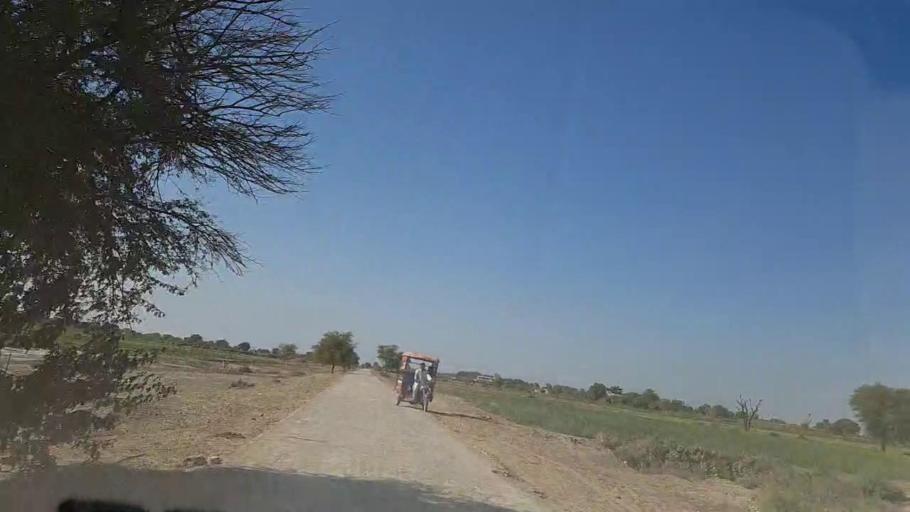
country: PK
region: Sindh
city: Digri
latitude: 25.1206
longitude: 69.0782
